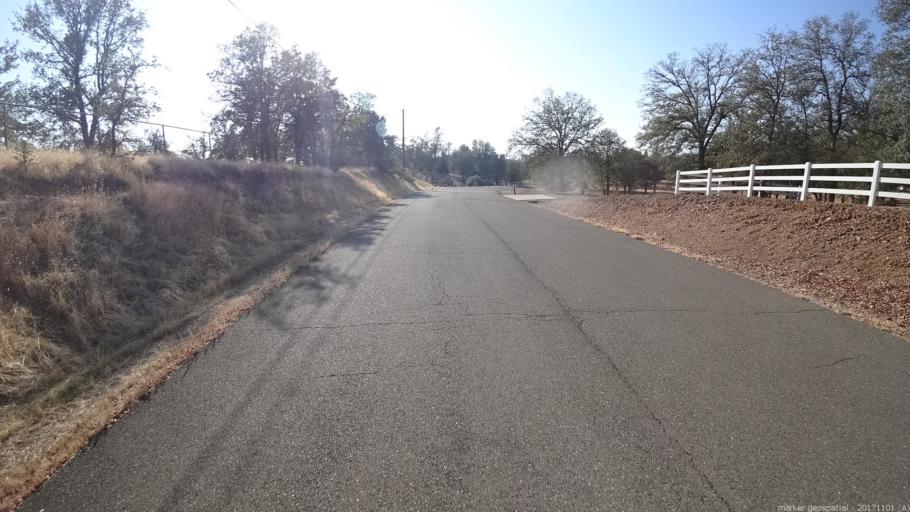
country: US
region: California
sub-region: Shasta County
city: Bella Vista
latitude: 40.6763
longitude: -122.2957
